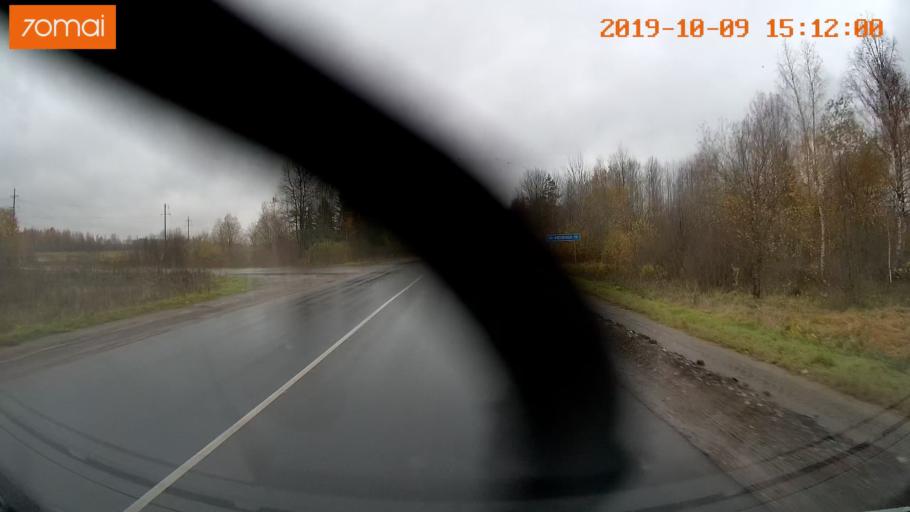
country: RU
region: Kostroma
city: Susanino
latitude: 58.1583
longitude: 41.6252
